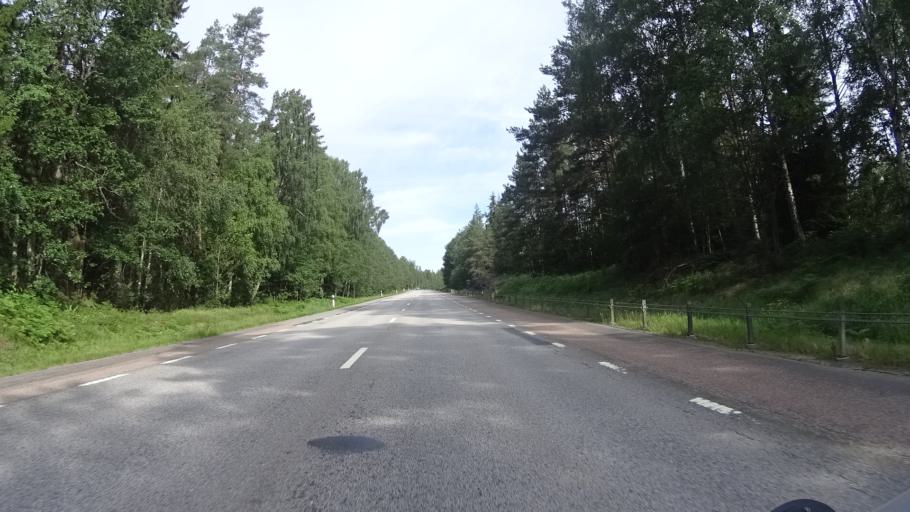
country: SE
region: Kalmar
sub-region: Vasterviks Kommun
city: Ankarsrum
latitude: 57.6213
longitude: 16.4649
